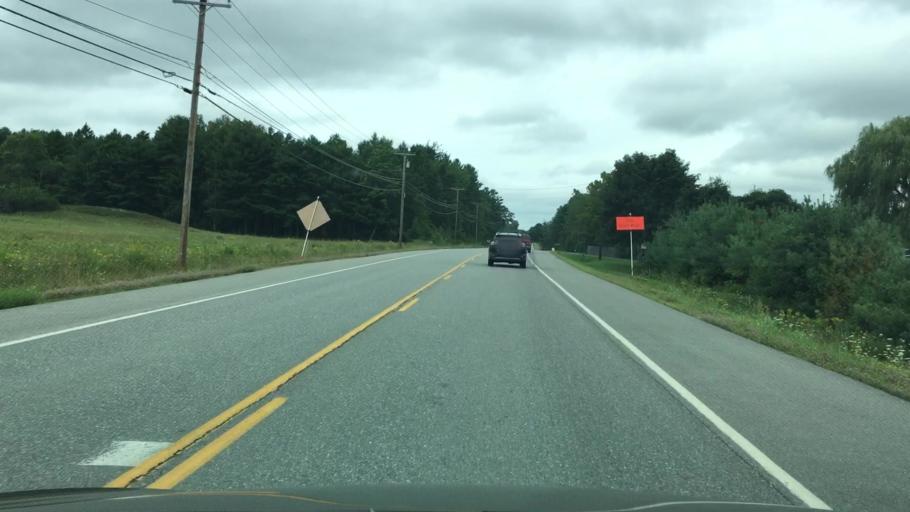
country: US
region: Maine
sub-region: Penobscot County
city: Orrington
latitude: 44.7040
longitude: -68.8226
